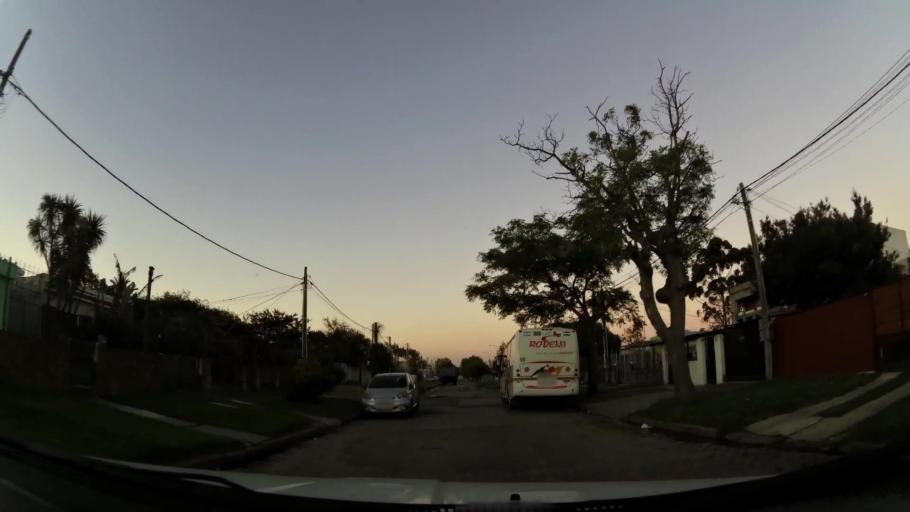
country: UY
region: Canelones
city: Toledo
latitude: -34.8156
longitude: -56.1403
